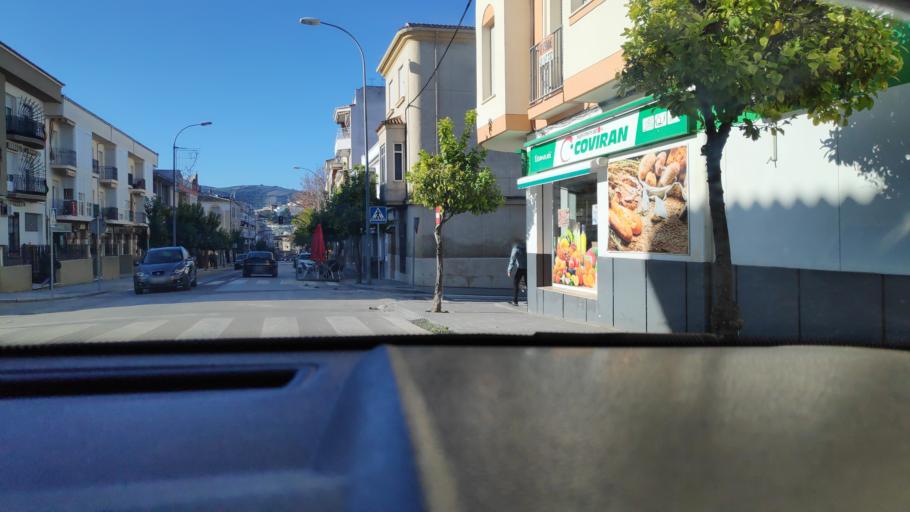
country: ES
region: Andalusia
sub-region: Province of Cordoba
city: Baena
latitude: 37.6178
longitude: -4.3184
